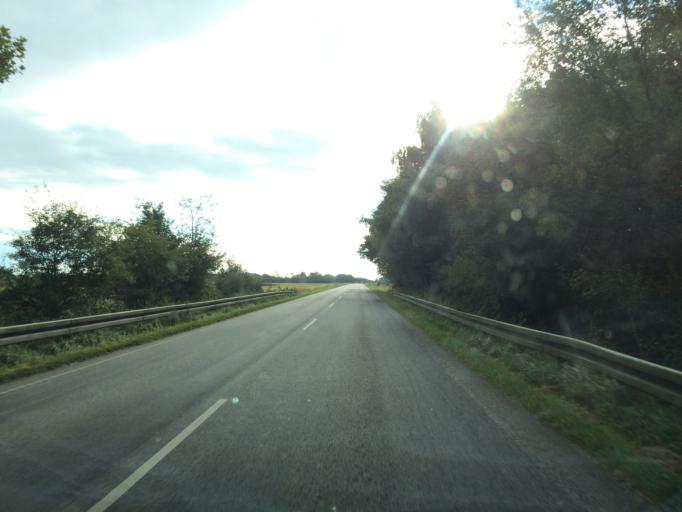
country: DK
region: Central Jutland
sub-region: Herning Kommune
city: Kibaek
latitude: 55.9472
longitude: 8.7553
